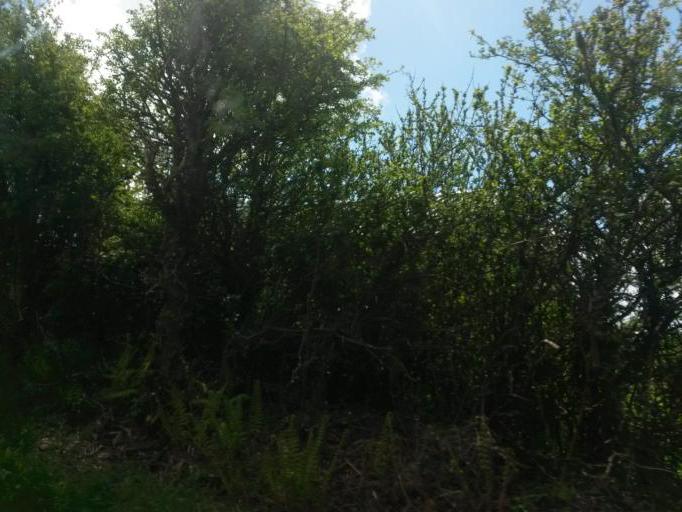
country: IE
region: Munster
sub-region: Waterford
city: Dunmore East
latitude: 52.2121
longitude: -6.9042
